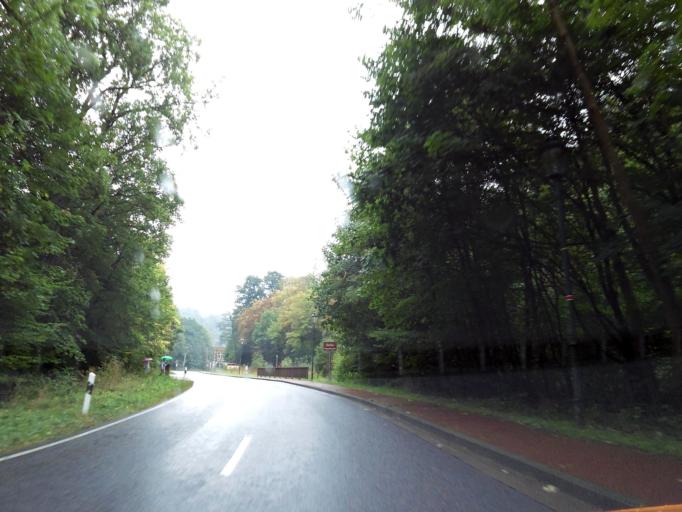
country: DE
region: Saxony-Anhalt
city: Harzgerode
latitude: 51.6547
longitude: 11.1168
